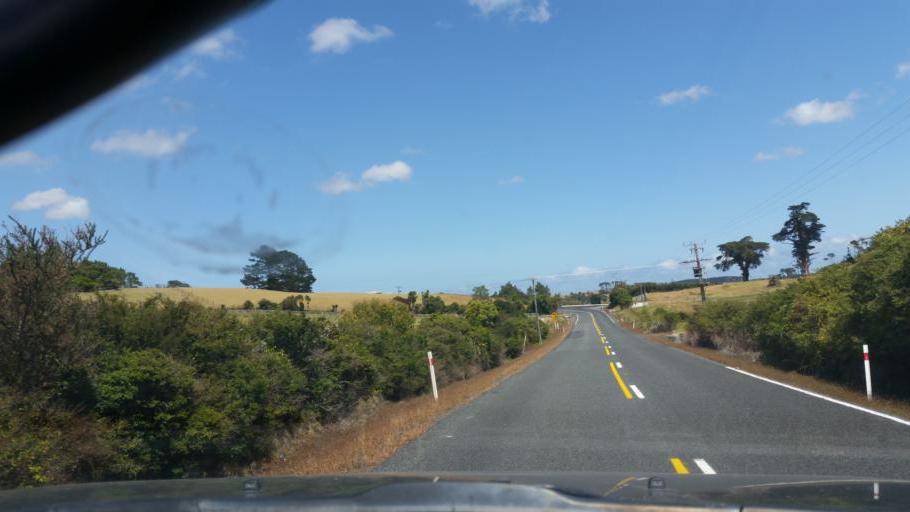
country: NZ
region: Northland
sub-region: Kaipara District
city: Dargaville
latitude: -35.9088
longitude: 173.8438
